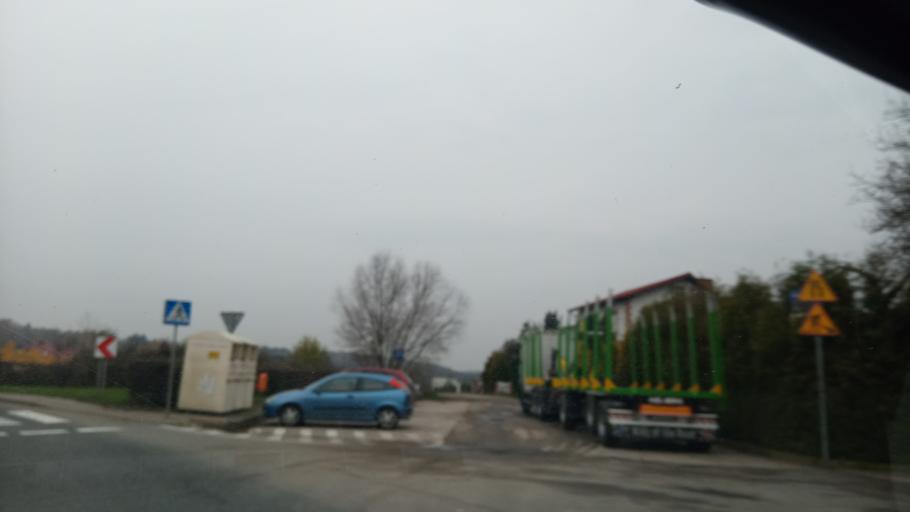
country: PL
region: Kujawsko-Pomorskie
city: Kamien Krajenski
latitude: 53.5330
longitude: 17.5150
